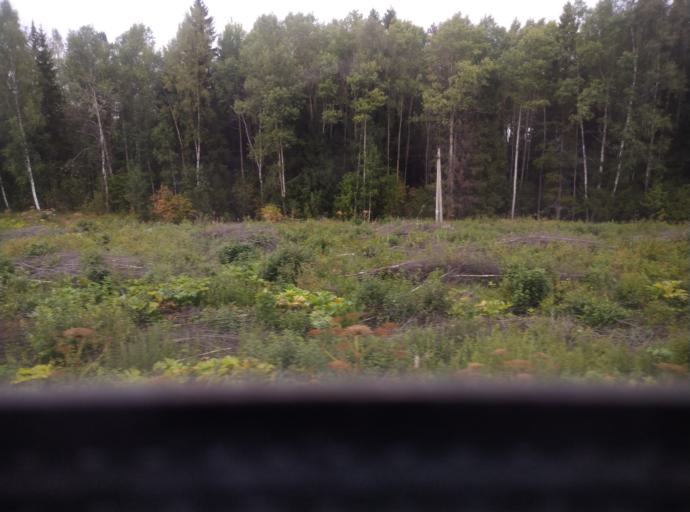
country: RU
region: Kostroma
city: Nerekhta
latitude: 57.4413
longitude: 40.4093
